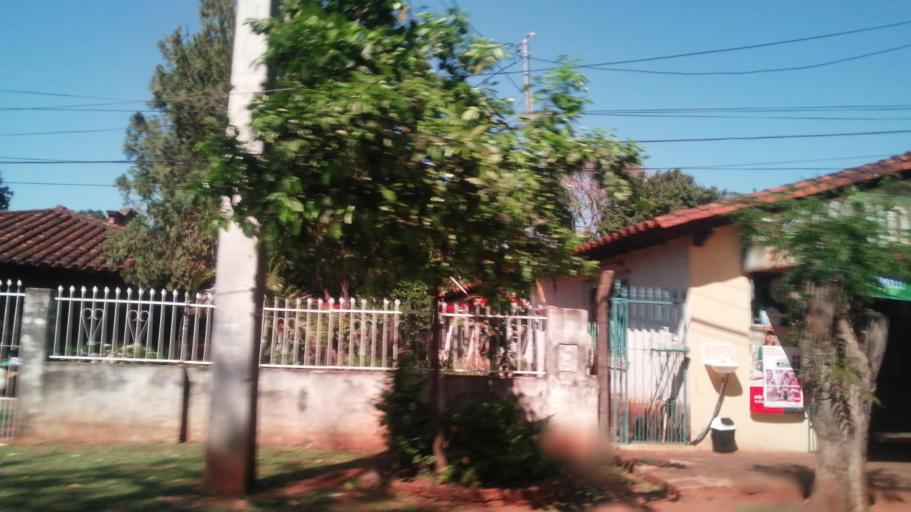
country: PY
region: Misiones
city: San Juan Bautista
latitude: -26.6724
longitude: -57.1317
